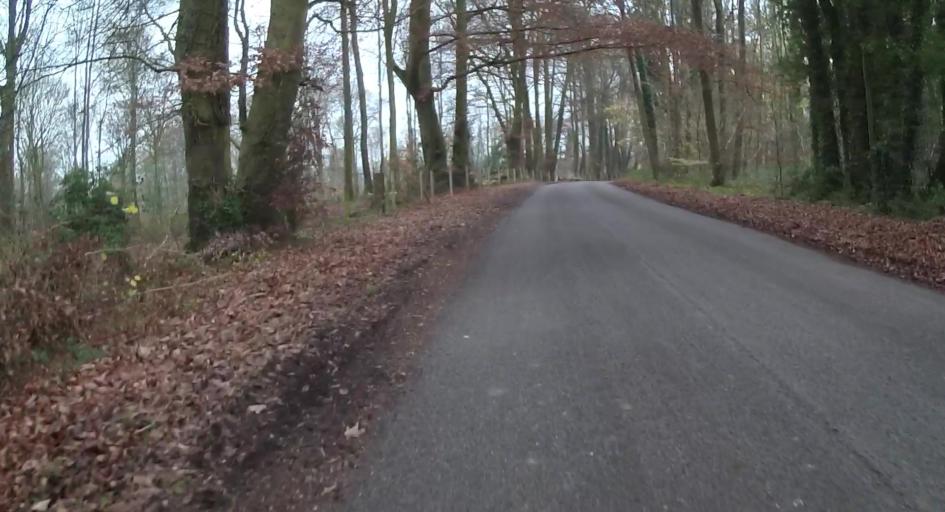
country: GB
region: England
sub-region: Hampshire
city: Kings Worthy
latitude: 51.1181
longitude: -1.2108
